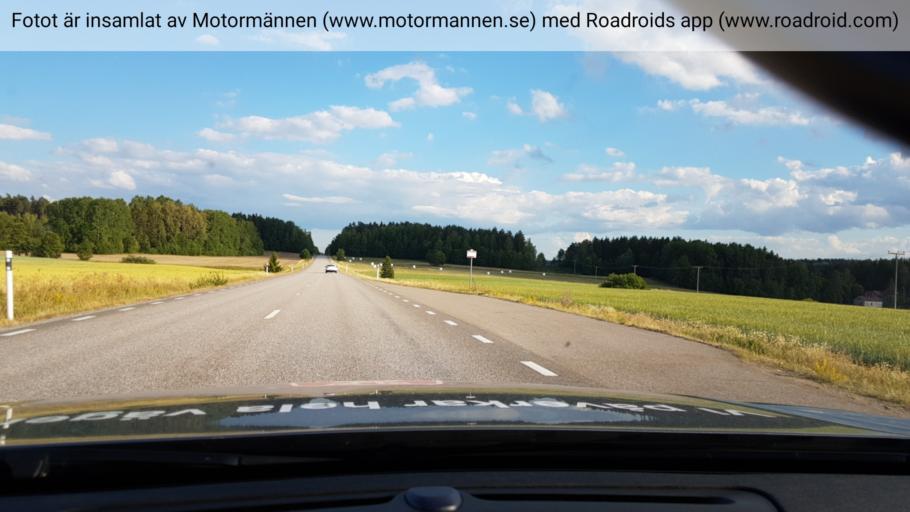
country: SE
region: Uppsala
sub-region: Heby Kommun
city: Heby
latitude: 59.9174
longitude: 16.8847
